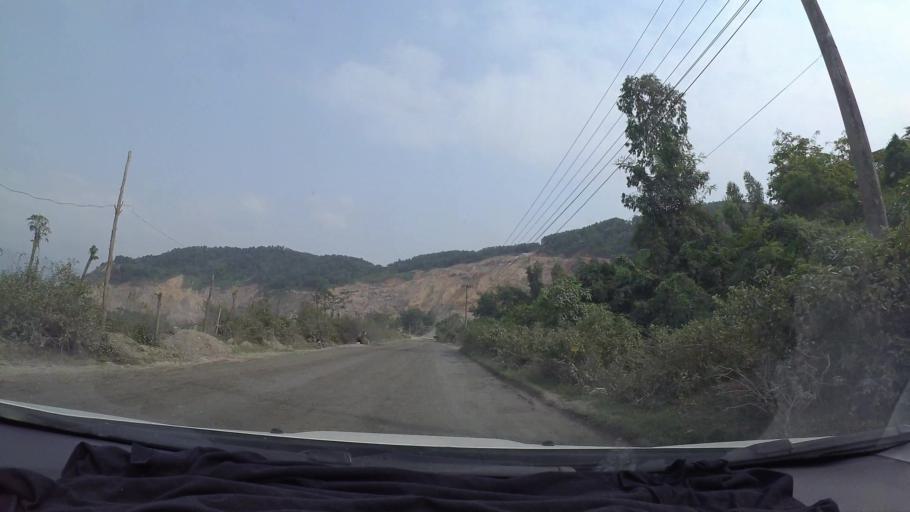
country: VN
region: Da Nang
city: Lien Chieu
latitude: 16.0403
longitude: 108.1512
